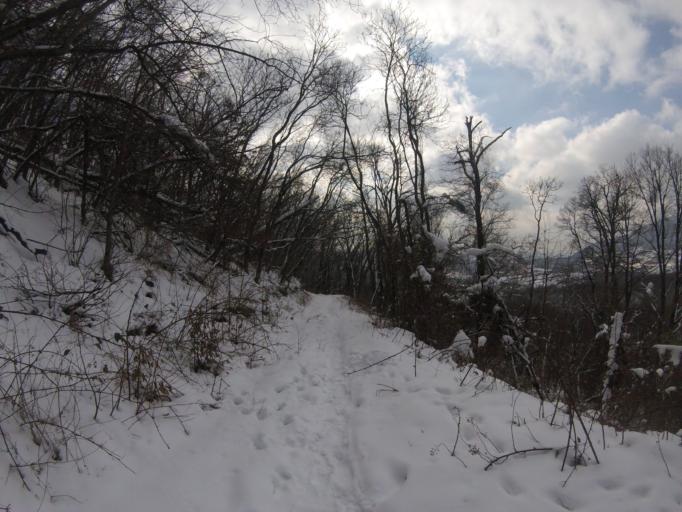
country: HU
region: Pest
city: Pilisszentkereszt
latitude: 47.7026
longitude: 18.9010
